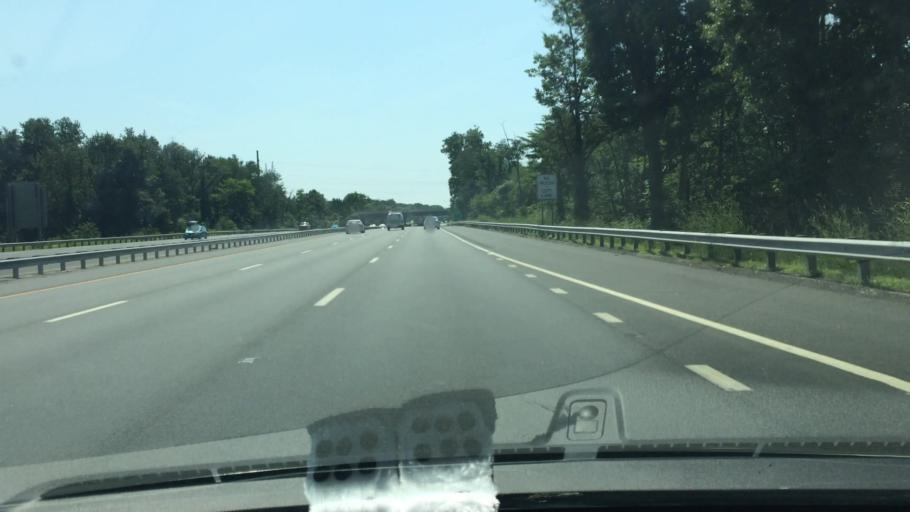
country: US
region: New Jersey
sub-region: Gloucester County
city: Gibbstown
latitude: 39.8089
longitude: -75.2854
